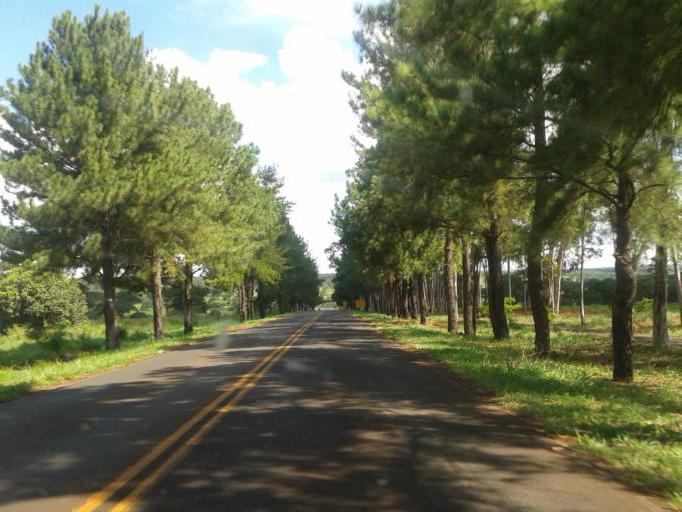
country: BR
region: Minas Gerais
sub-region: Santa Vitoria
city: Santa Vitoria
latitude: -18.8717
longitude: -50.1236
